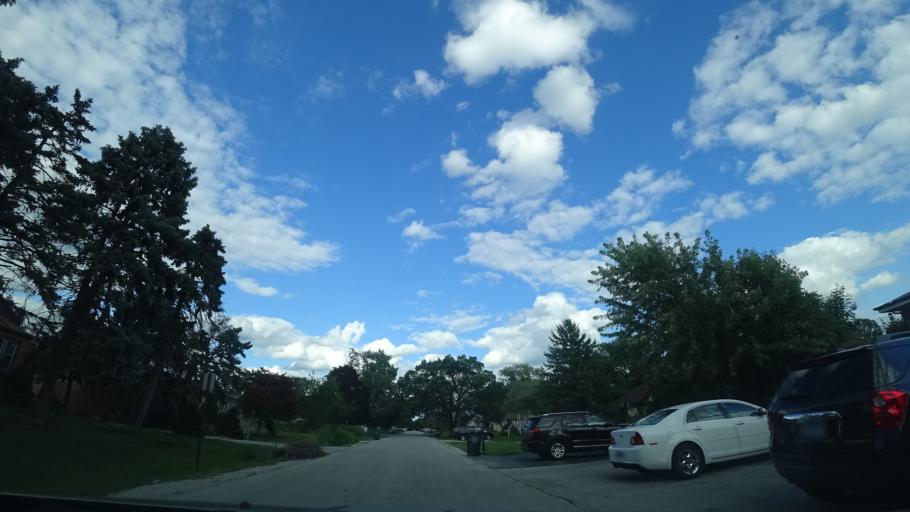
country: US
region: Illinois
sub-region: Cook County
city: Merrionette Park
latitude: 41.6832
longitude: -87.7162
